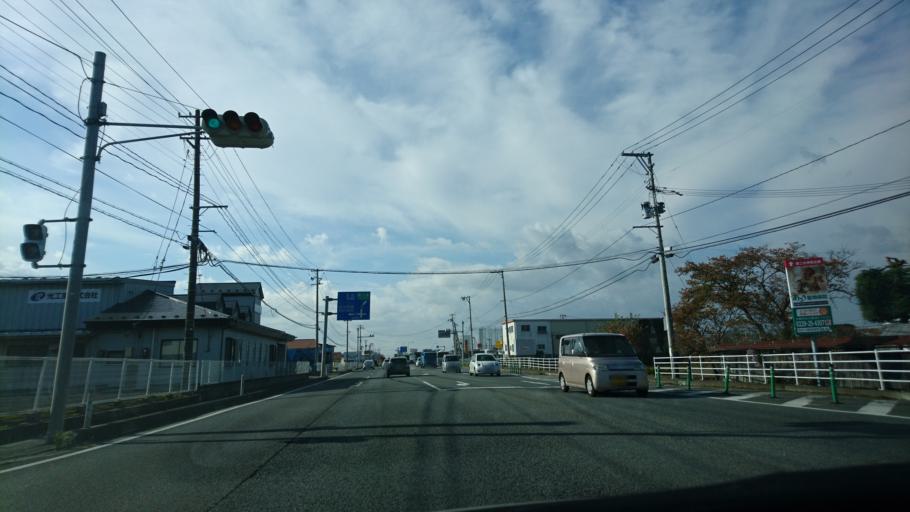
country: JP
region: Miyagi
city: Furukawa
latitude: 38.6063
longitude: 140.9817
